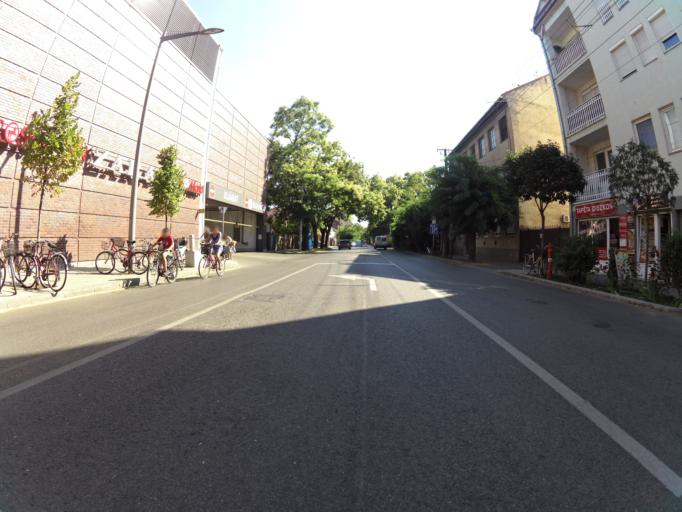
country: HU
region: Csongrad
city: Szeged
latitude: 46.2551
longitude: 20.1364
